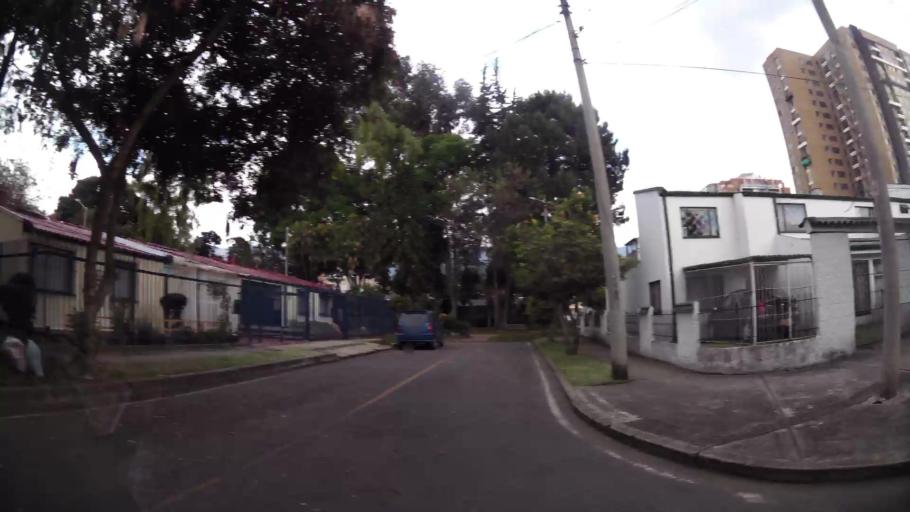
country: CO
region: Bogota D.C.
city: Barrio San Luis
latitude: 4.7285
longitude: -74.0364
